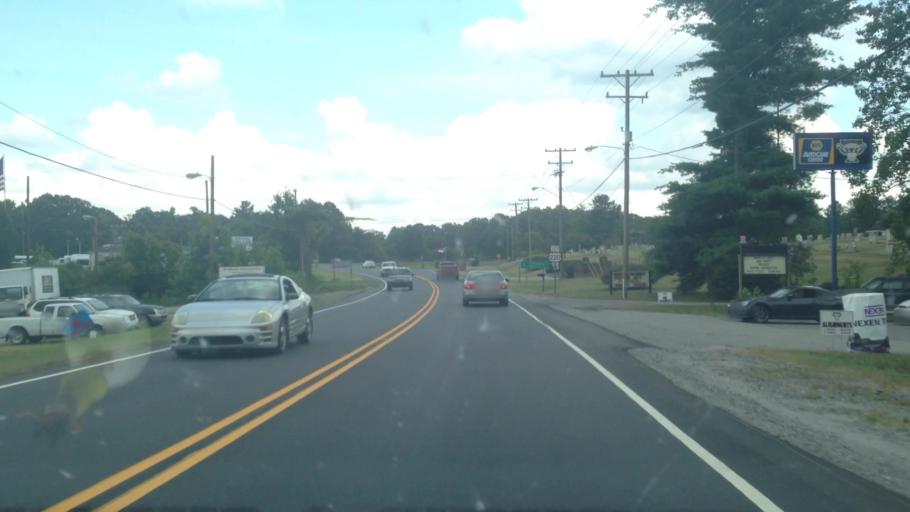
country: US
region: North Carolina
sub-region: Rockingham County
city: Madison
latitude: 36.3769
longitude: -79.9457
